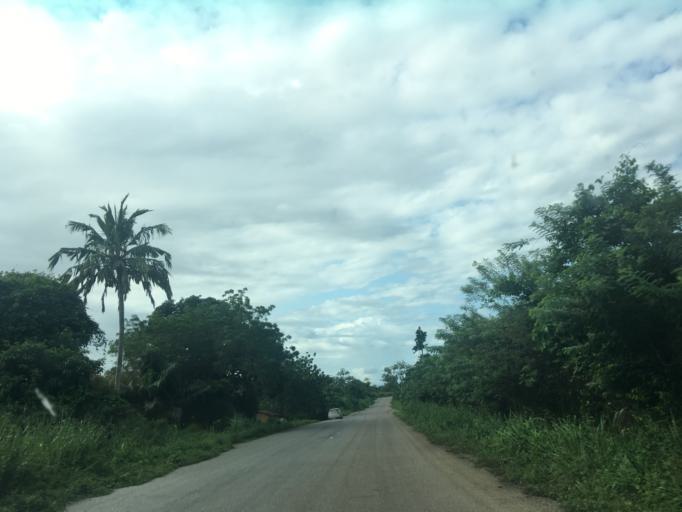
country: GH
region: Western
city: Wassa-Akropong
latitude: 6.0180
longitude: -2.4030
